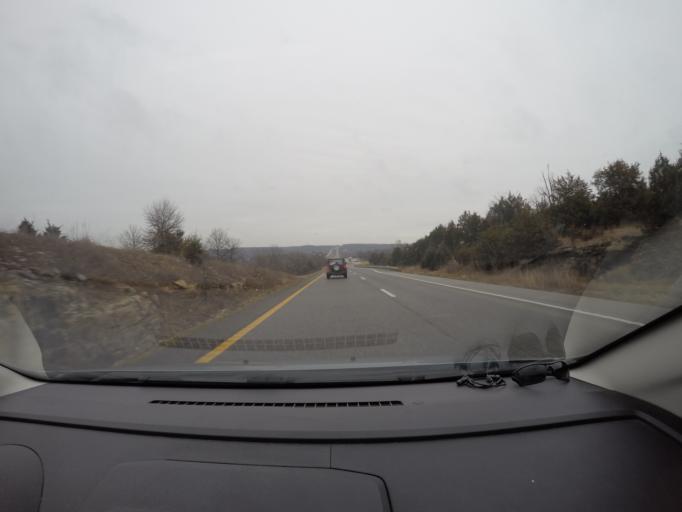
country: US
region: Missouri
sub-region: Montgomery County
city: Montgomery City
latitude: 38.8961
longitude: -91.6060
